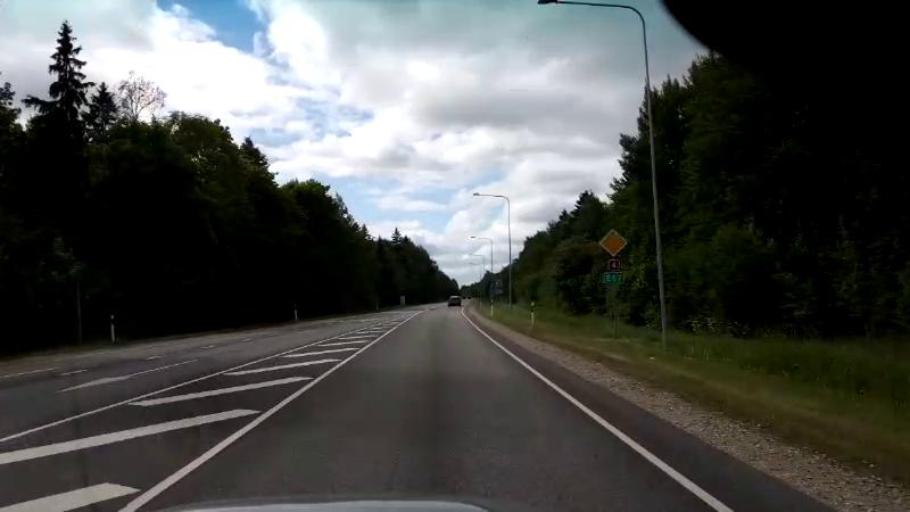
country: EE
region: Paernumaa
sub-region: Halinga vald
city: Parnu-Jaagupi
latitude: 58.6102
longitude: 24.5125
